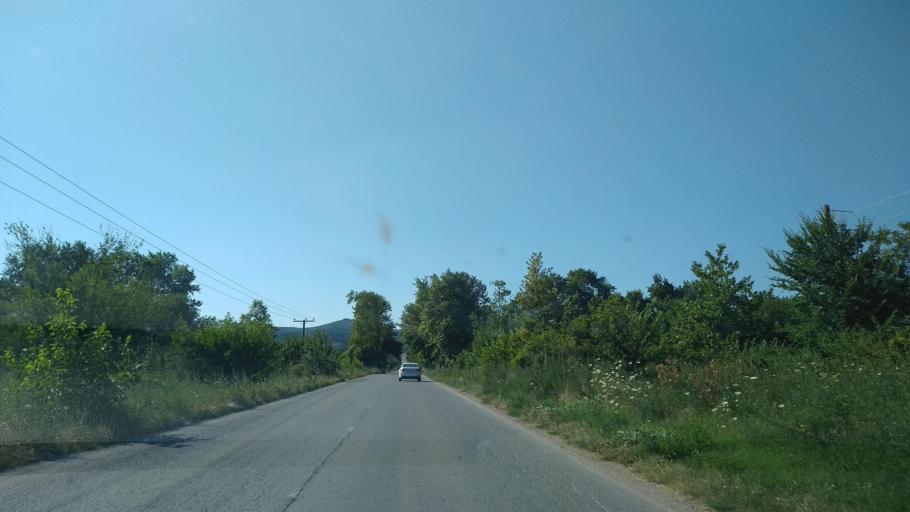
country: GR
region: Central Macedonia
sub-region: Nomos Chalkidikis
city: Megali Panagia
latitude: 40.4215
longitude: 23.6878
